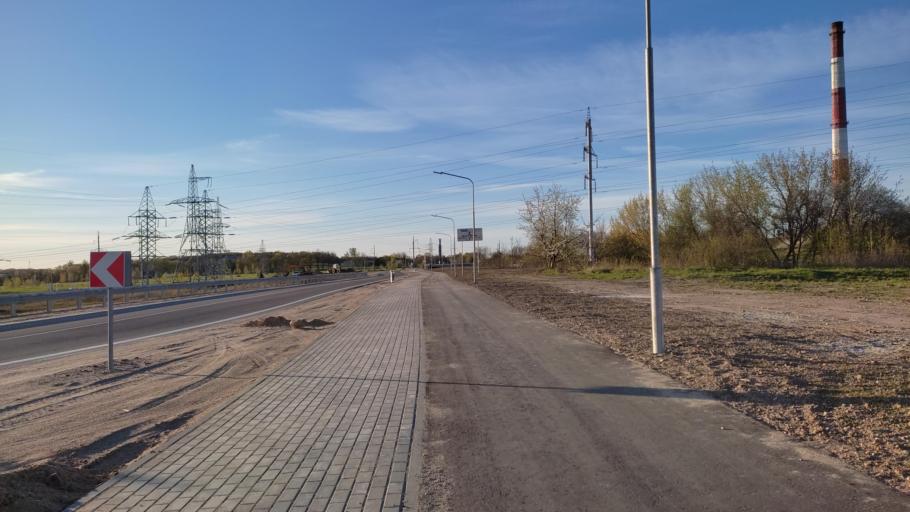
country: BY
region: Grodnenskaya
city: Hrodna
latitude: 53.6667
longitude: 23.8916
